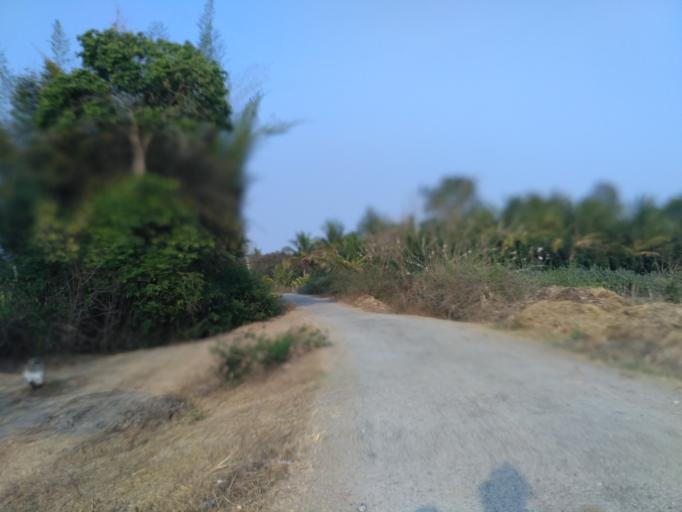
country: IN
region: Karnataka
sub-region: Hassan
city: Alur
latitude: 12.9906
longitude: 76.0232
